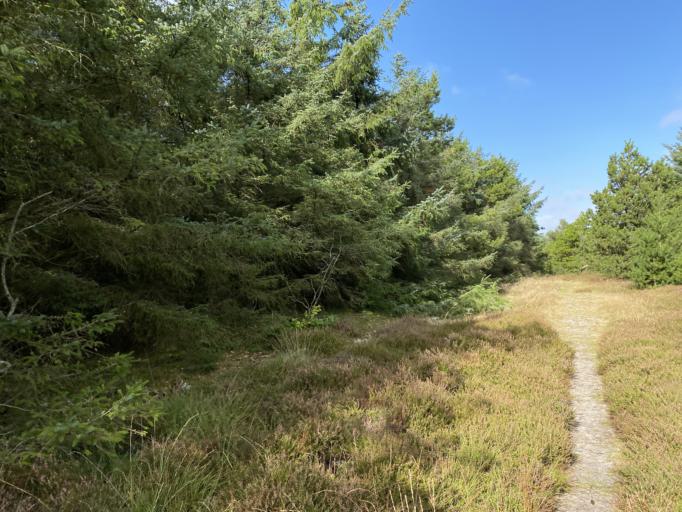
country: DK
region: Central Jutland
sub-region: Holstebro Kommune
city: Ulfborg
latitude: 56.3148
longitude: 8.1375
